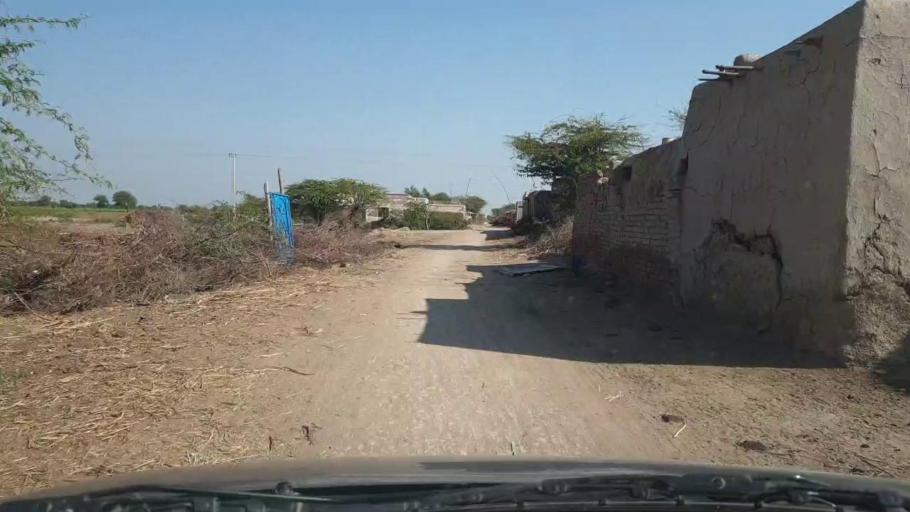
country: PK
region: Sindh
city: Samaro
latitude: 25.2012
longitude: 69.2630
